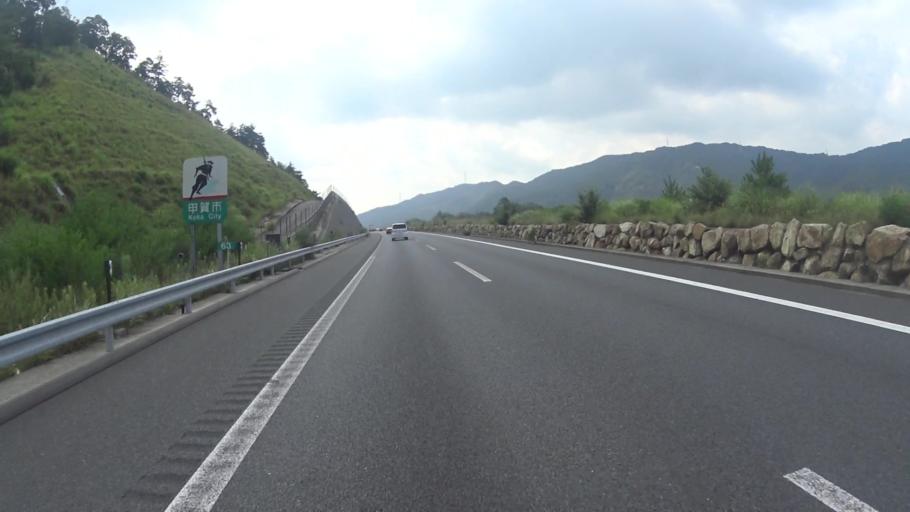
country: JP
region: Shiga Prefecture
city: Kusatsu
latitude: 34.9385
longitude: 136.0364
